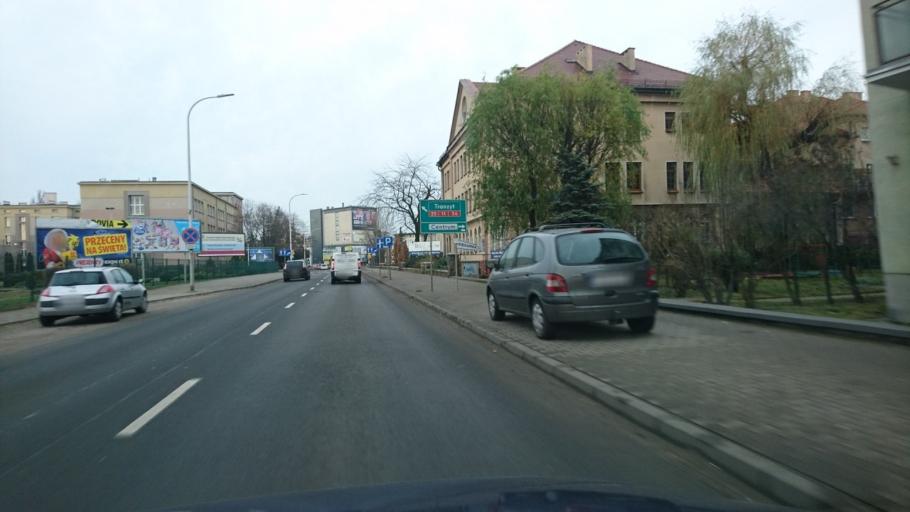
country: PL
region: Greater Poland Voivodeship
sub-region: Powiat ostrowski
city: Ostrow Wielkopolski
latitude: 51.6519
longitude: 17.8095
